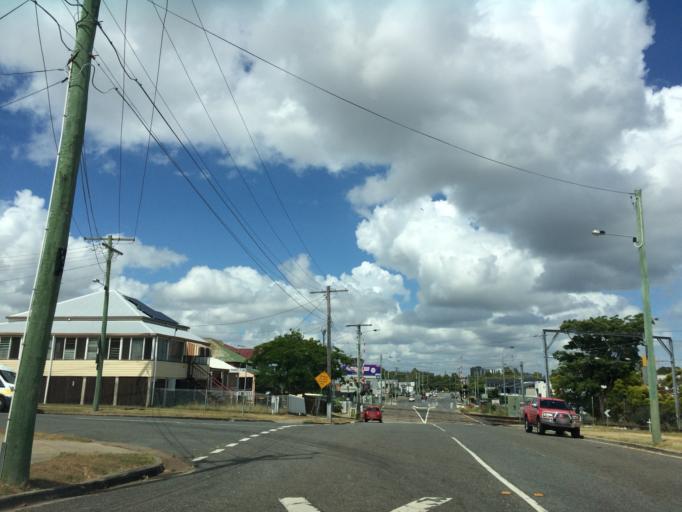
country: AU
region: Queensland
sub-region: Brisbane
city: Seven Hills
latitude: -27.4857
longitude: 153.0575
